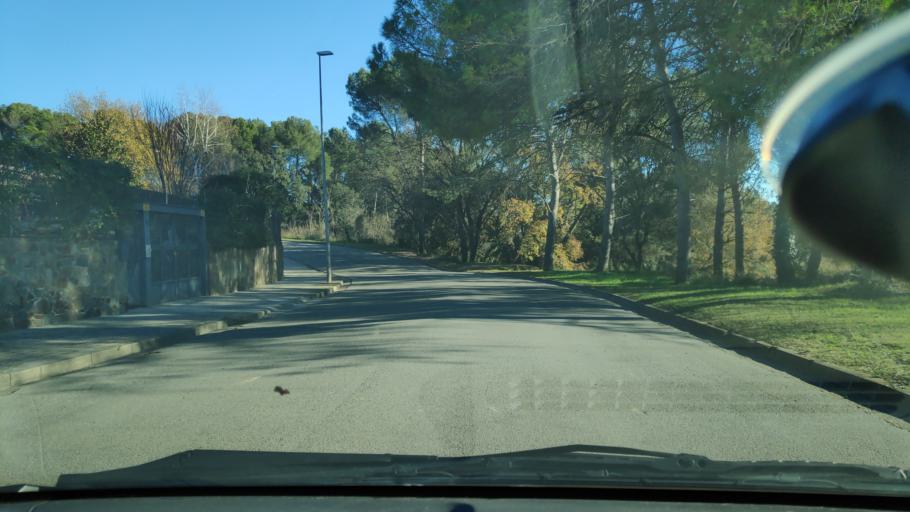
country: ES
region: Catalonia
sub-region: Provincia de Barcelona
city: Sant Quirze del Valles
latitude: 41.5365
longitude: 2.0645
